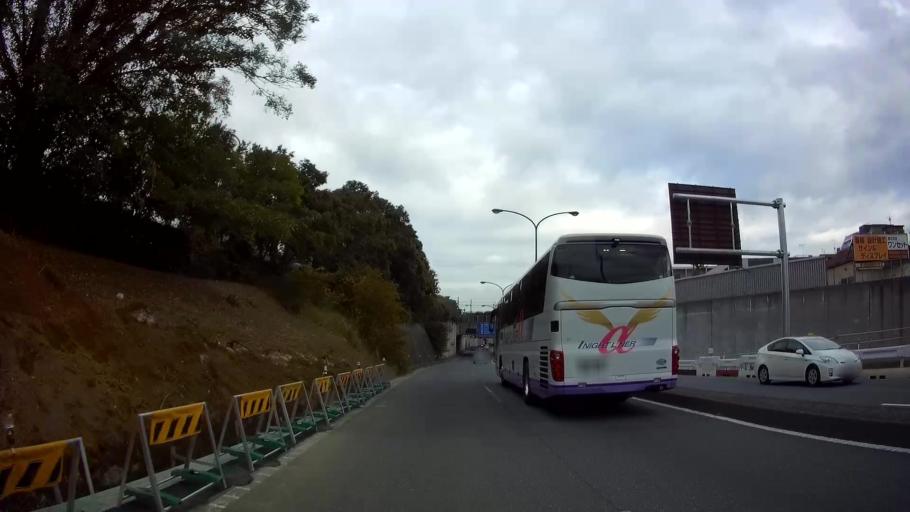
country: JP
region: Saitama
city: Wako
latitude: 35.7675
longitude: 139.6528
